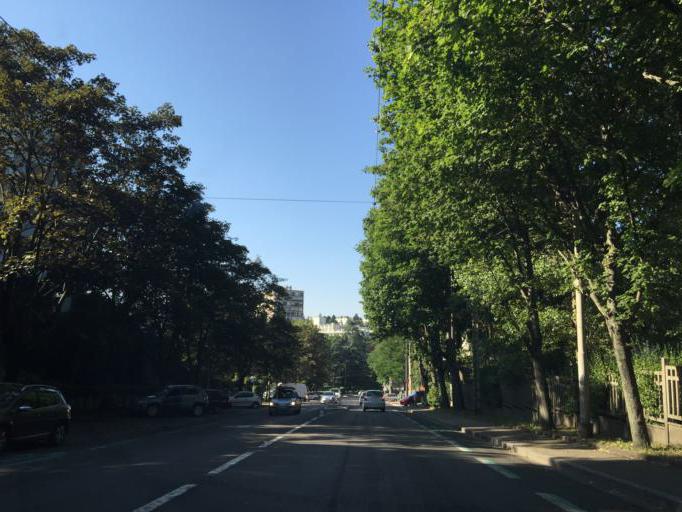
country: FR
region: Rhone-Alpes
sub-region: Departement de la Loire
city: Saint-Etienne
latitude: 45.4185
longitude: 4.4114
